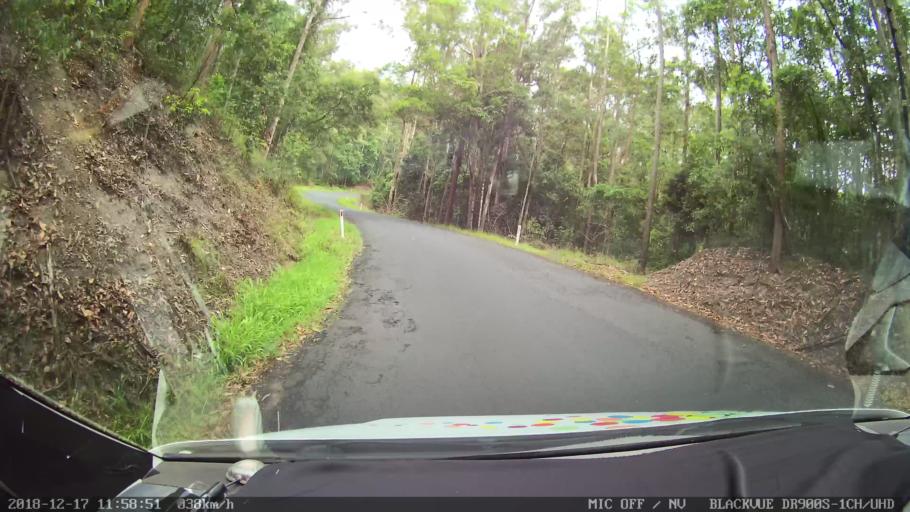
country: AU
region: New South Wales
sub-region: Kyogle
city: Kyogle
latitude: -28.5337
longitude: 152.5696
